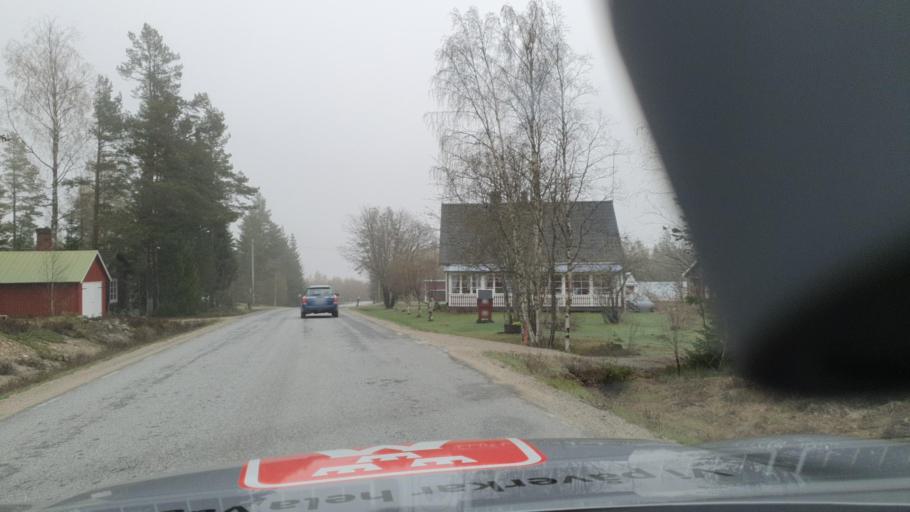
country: SE
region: Vaesternorrland
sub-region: OErnskoeldsviks Kommun
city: Husum
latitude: 63.4811
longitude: 19.2112
